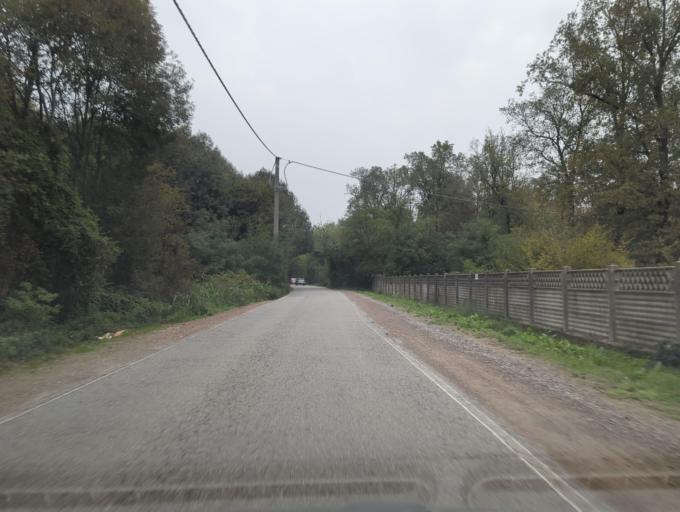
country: IT
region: Lombardy
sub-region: Citta metropolitana di Milano
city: Nosate
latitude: 45.5578
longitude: 8.7389
